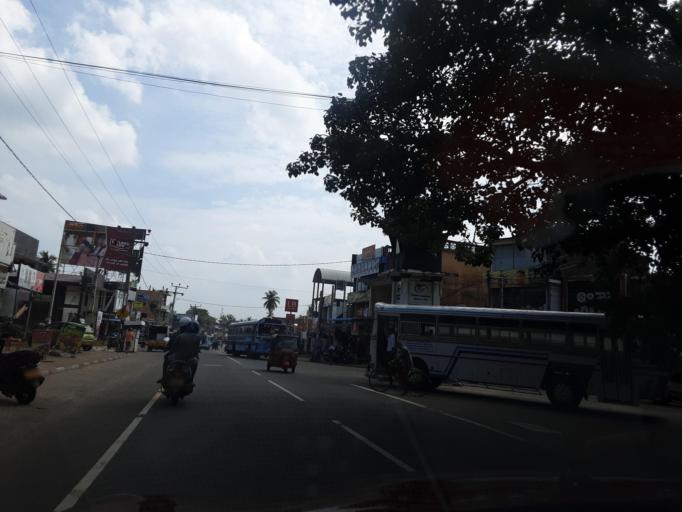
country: LK
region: Northern Province
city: Vavuniya
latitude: 8.5388
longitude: 80.4931
